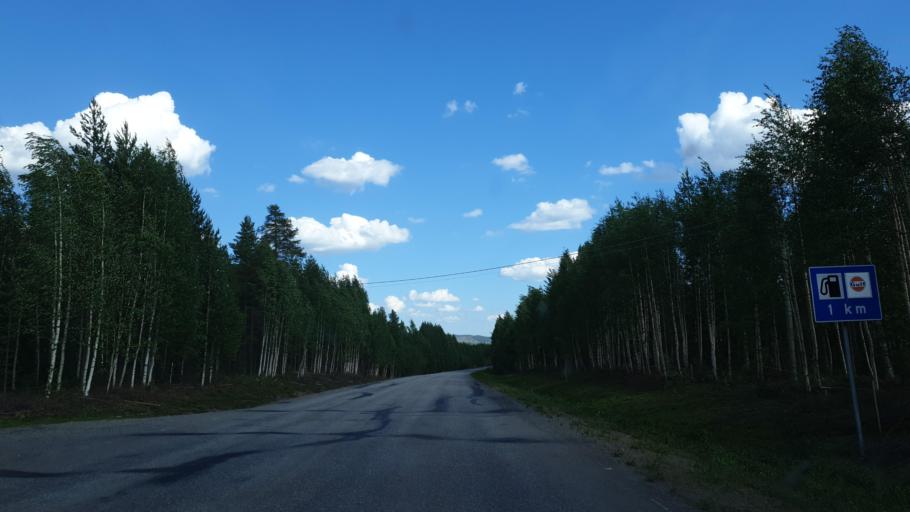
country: SE
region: Norrbotten
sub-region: Alvsbyns Kommun
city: AElvsbyn
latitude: 65.8441
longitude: 20.4905
